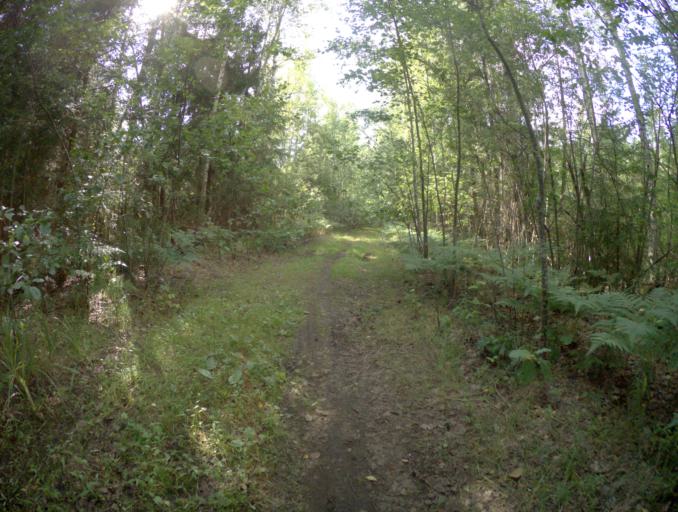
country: RU
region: Vladimir
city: Sobinka
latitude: 55.9135
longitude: 40.1050
